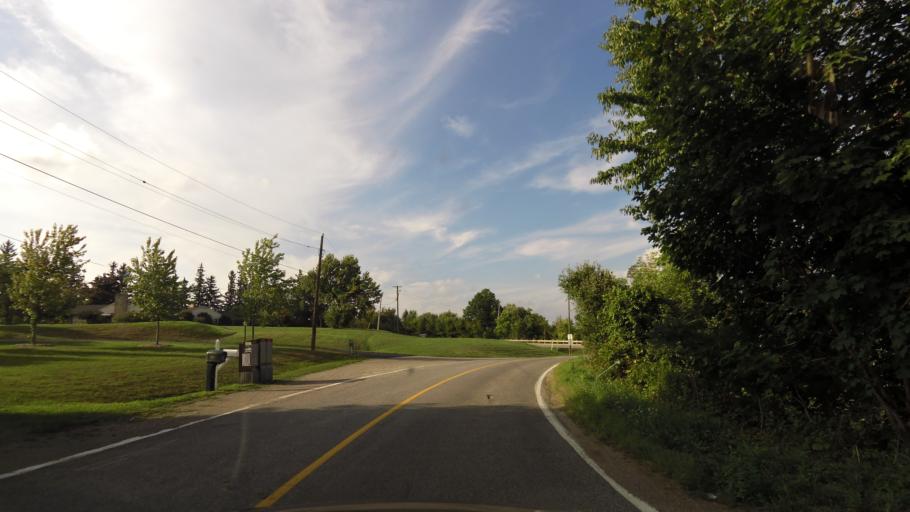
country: CA
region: Ontario
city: Burlington
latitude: 43.3925
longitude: -79.8611
